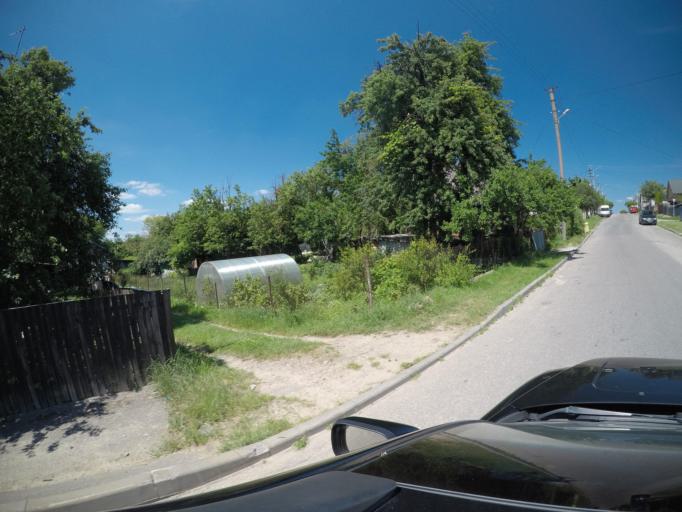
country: BY
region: Grodnenskaya
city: Hrodna
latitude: 53.6907
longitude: 23.8179
